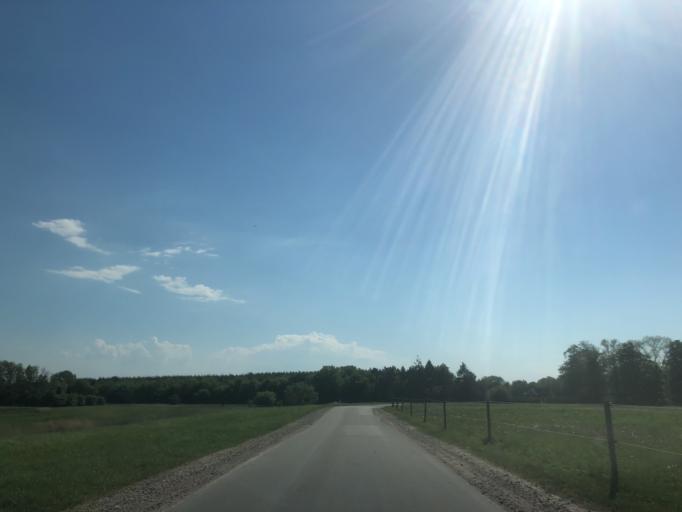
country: DK
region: Zealand
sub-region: Roskilde Kommune
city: Vindinge
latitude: 55.6187
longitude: 12.1192
